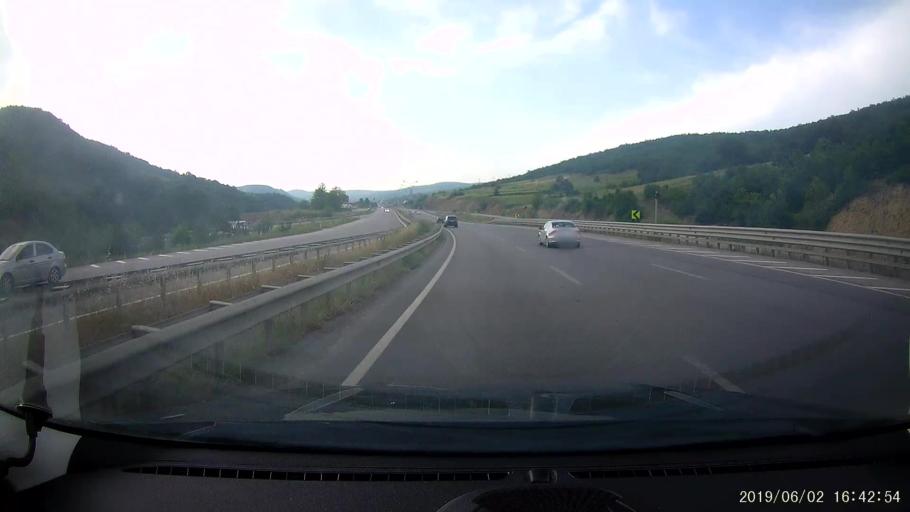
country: TR
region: Samsun
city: Kavak
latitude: 41.1261
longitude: 36.1379
